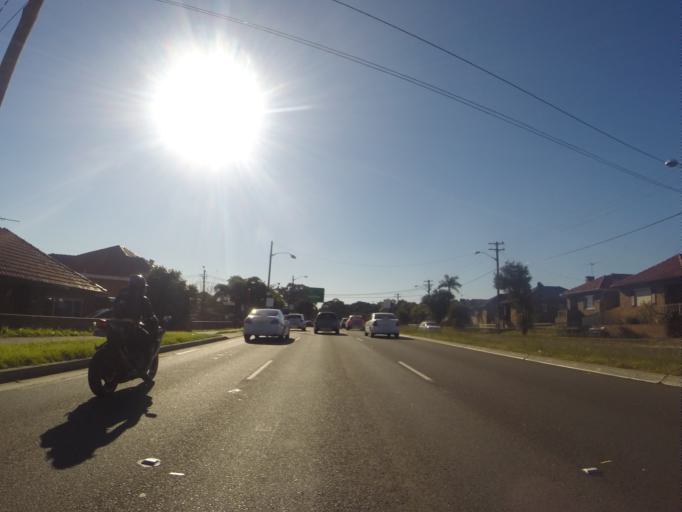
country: AU
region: New South Wales
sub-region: Canterbury
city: Roselands
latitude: -33.9318
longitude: 151.0729
